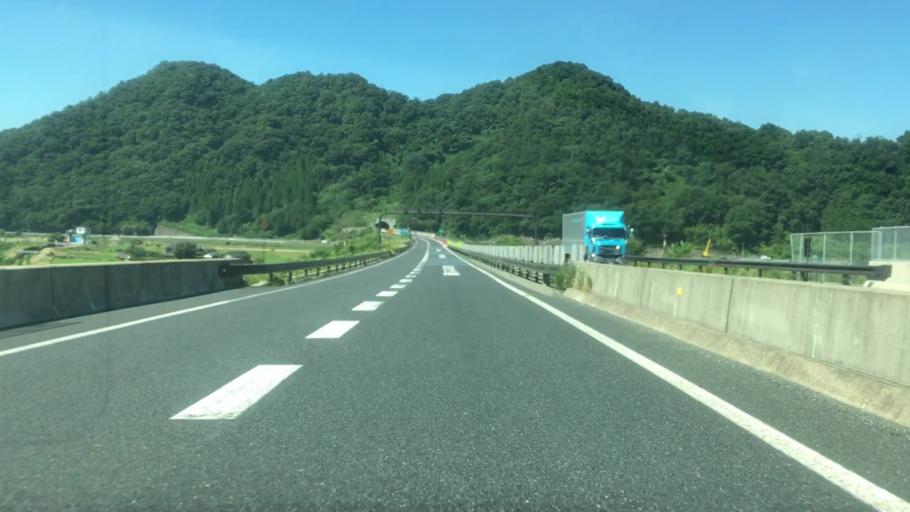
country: JP
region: Tottori
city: Tottori
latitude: 35.3752
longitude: 134.2042
